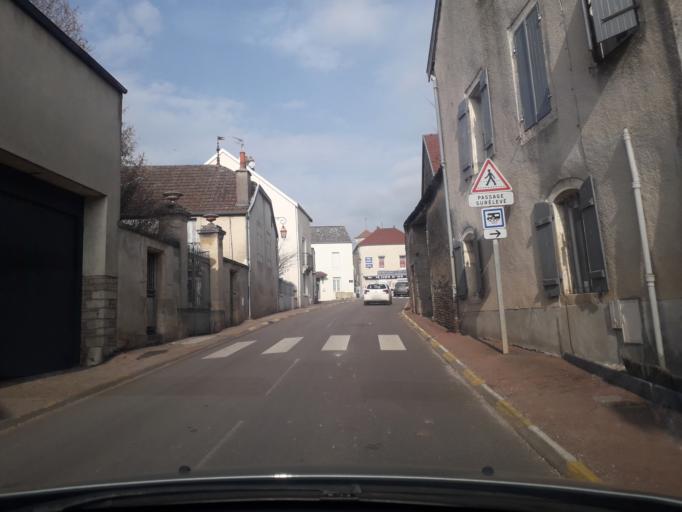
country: FR
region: Bourgogne
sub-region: Departement de la Cote-d'Or
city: Messigny-et-Vantoux
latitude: 47.4050
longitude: 5.0179
